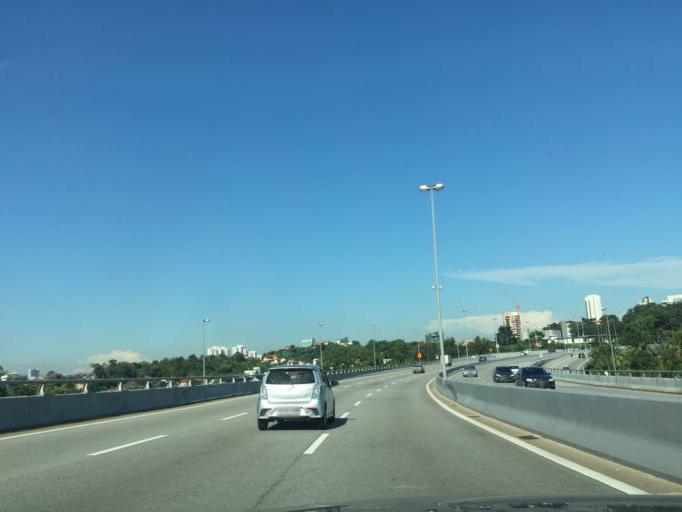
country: MY
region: Selangor
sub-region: Petaling
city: Petaling Jaya
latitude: 3.1596
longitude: 101.6269
